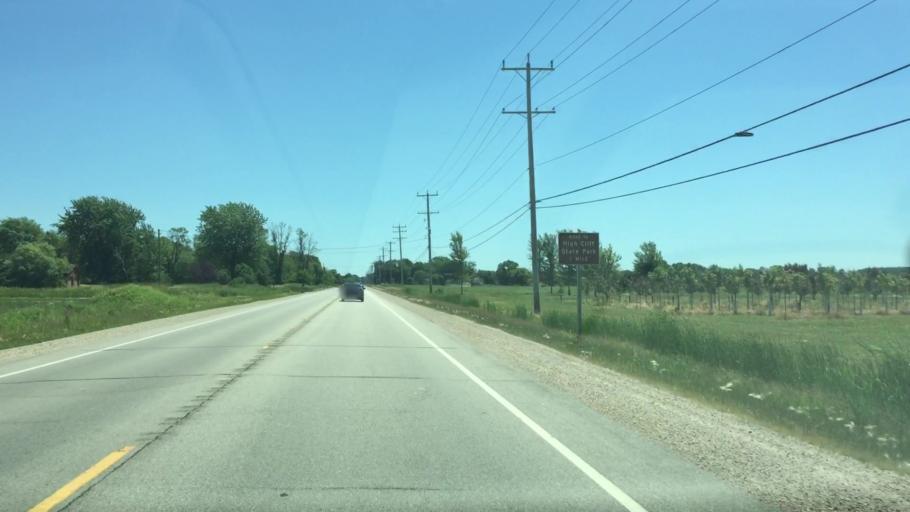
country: US
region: Wisconsin
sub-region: Calumet County
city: Sherwood
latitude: 44.1979
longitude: -88.3128
